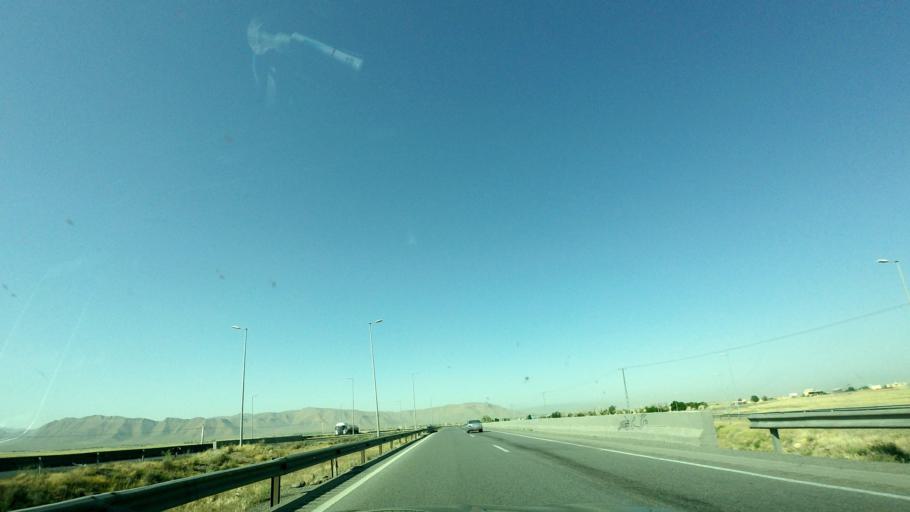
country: IR
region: Markazi
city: Arak
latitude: 34.1700
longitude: 50.0340
